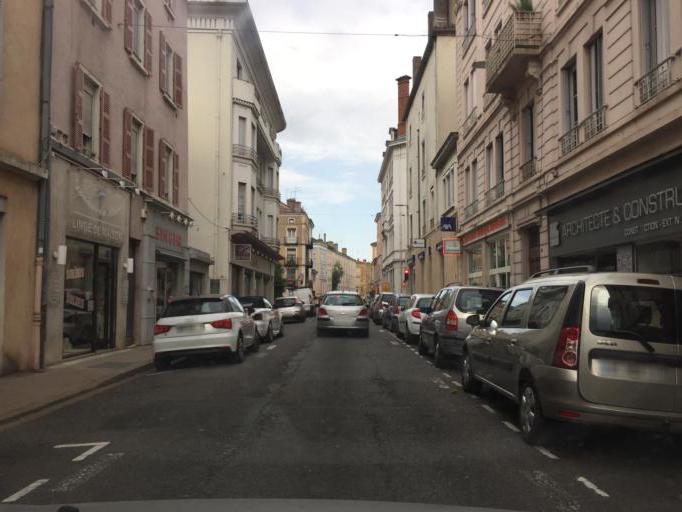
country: FR
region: Rhone-Alpes
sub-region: Departement du Rhone
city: Villefranche-sur-Saone
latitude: 45.9871
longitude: 4.7160
